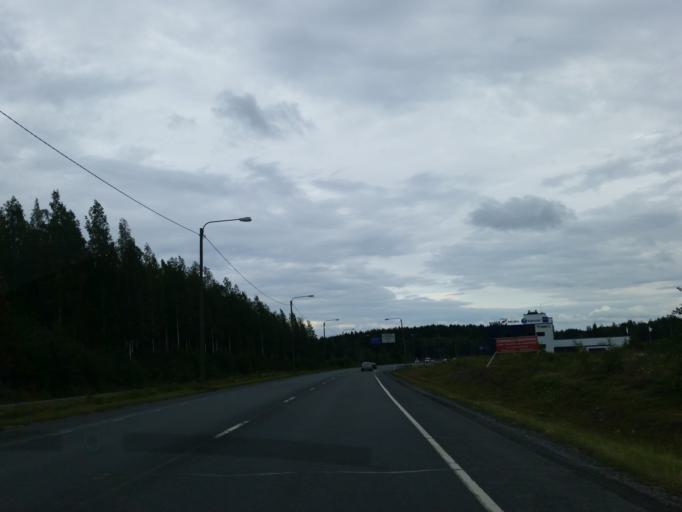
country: FI
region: Northern Savo
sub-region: Kuopio
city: Kuopio
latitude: 62.9858
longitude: 27.7643
